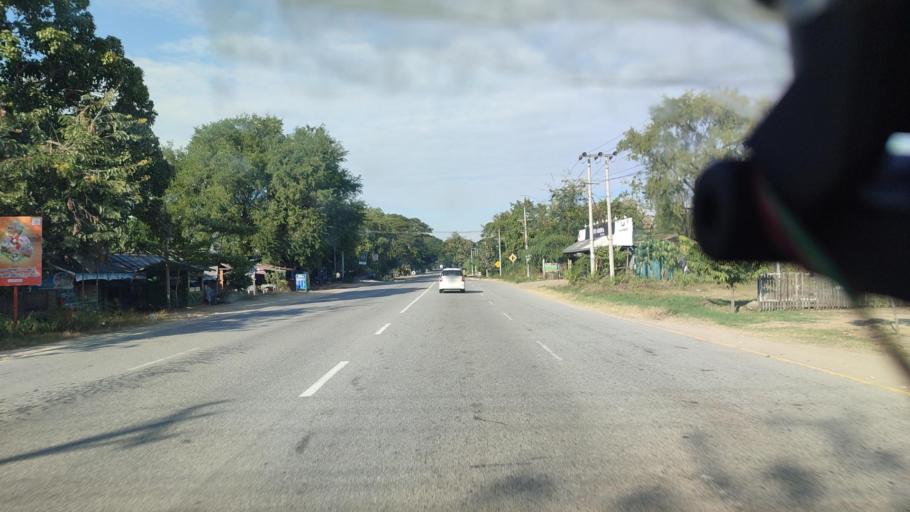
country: MM
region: Mandalay
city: Pyinmana
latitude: 20.0386
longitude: 96.2466
